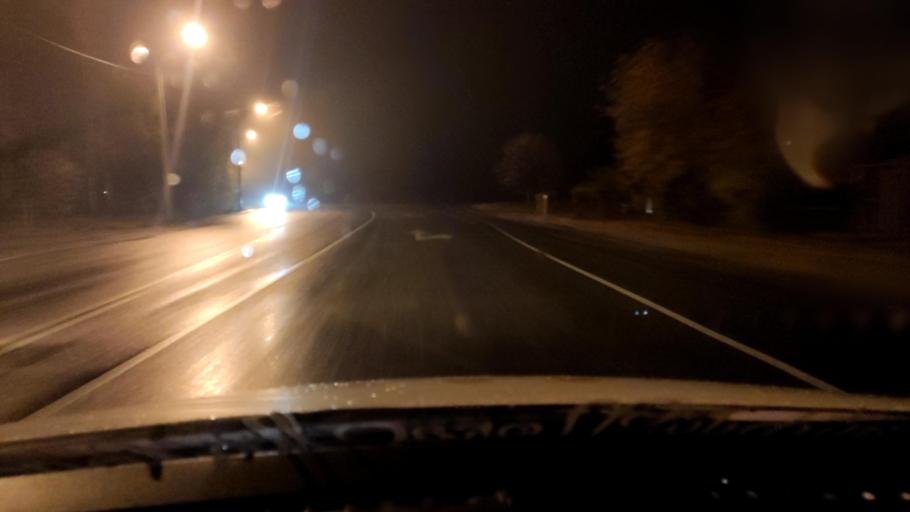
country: RU
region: Voronezj
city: Pridonskoy
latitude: 51.7005
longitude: 39.0786
